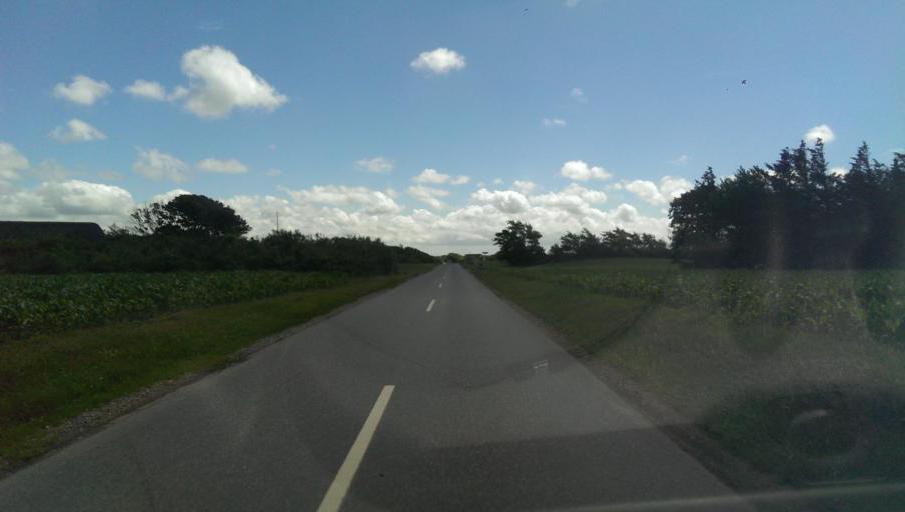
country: DK
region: Central Jutland
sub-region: Holstebro Kommune
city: Ulfborg
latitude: 56.2419
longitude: 8.1888
